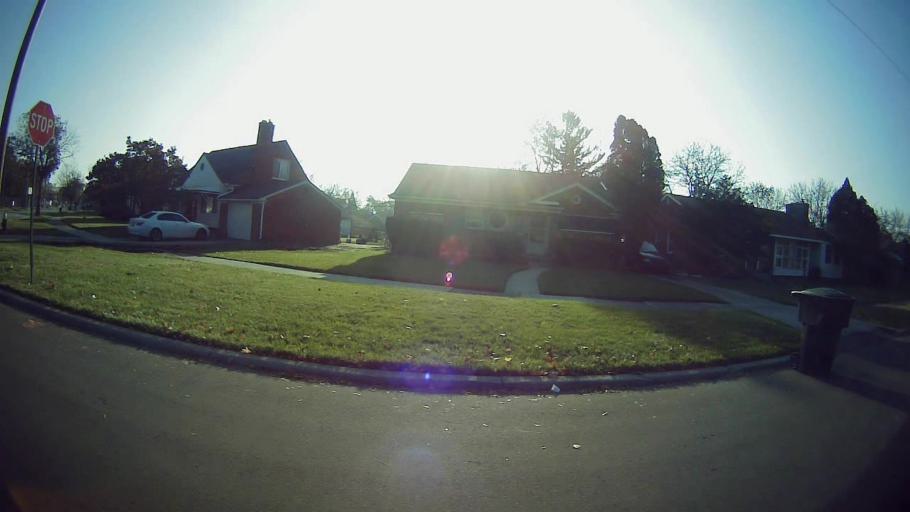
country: US
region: Michigan
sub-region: Wayne County
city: Dearborn
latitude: 42.3624
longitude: -83.1572
